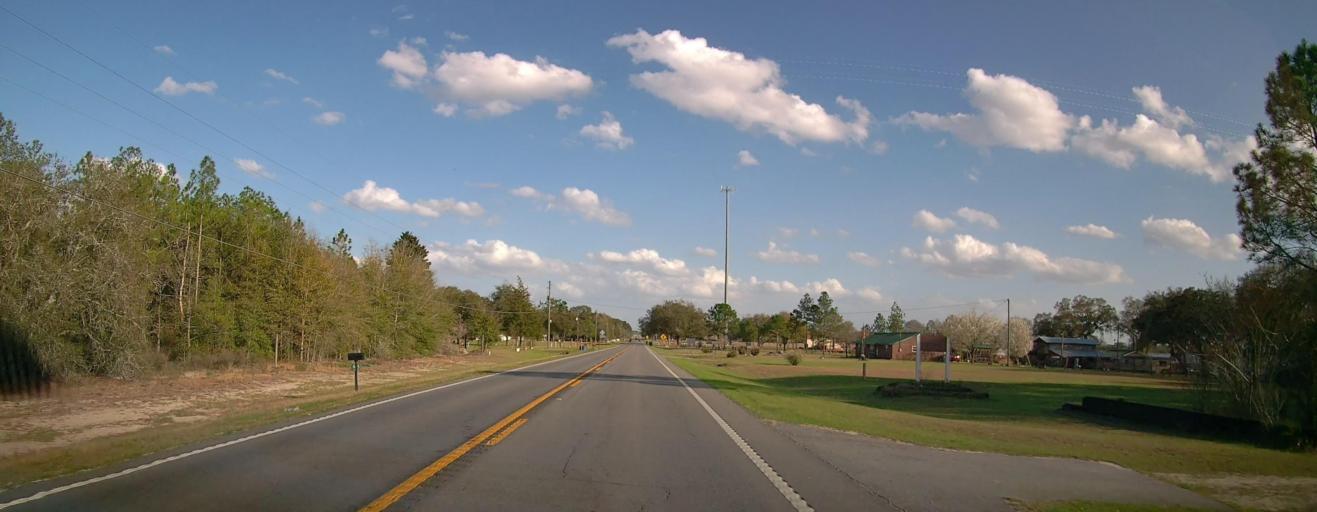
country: US
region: Georgia
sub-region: Tattnall County
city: Reidsville
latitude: 32.1142
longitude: -82.1836
